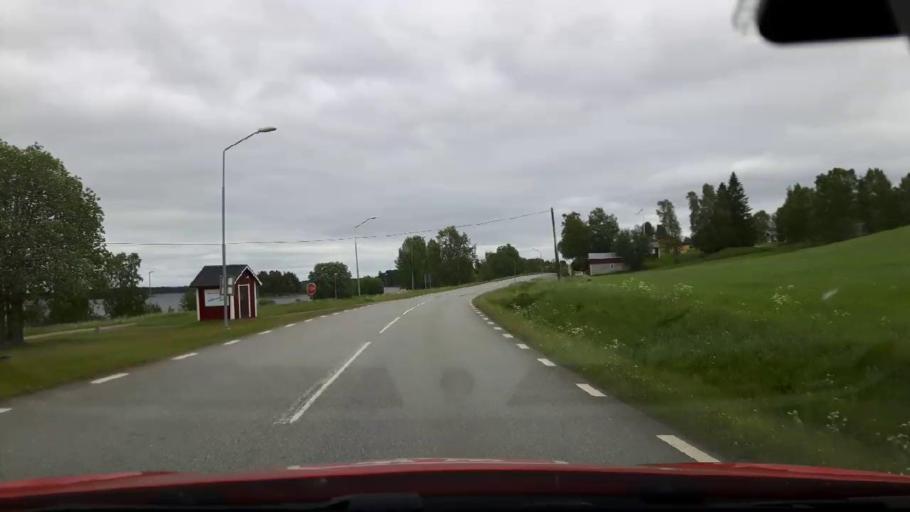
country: SE
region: Jaemtland
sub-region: Stroemsunds Kommun
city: Stroemsund
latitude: 63.5801
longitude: 15.3628
